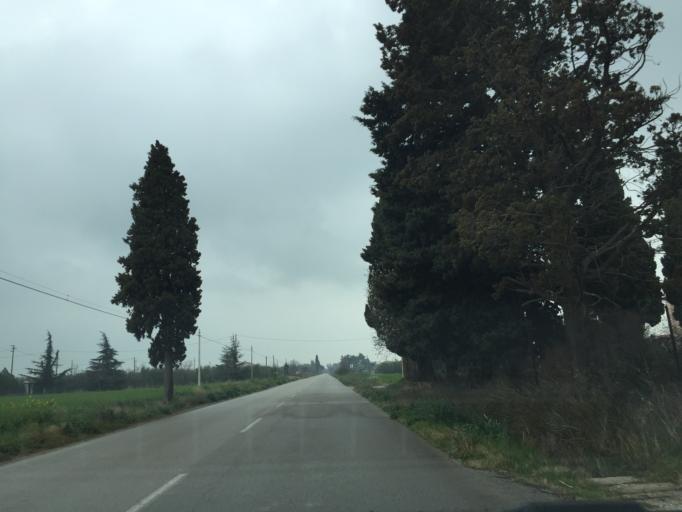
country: IT
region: Apulia
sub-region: Provincia di Foggia
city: Foggia
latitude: 41.4177
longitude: 15.4593
